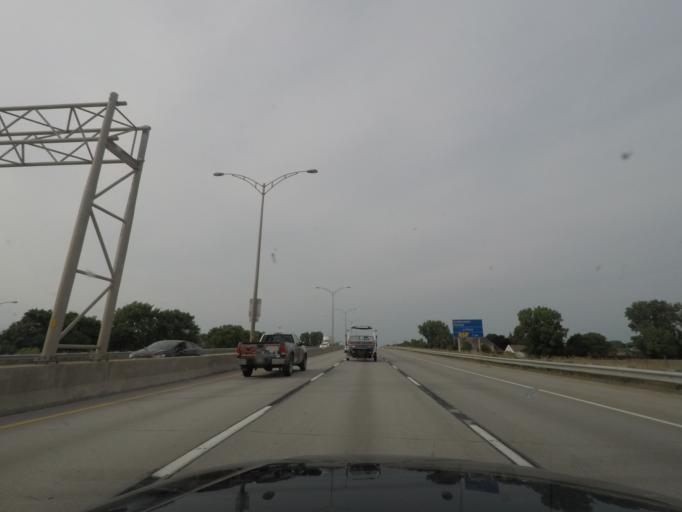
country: CA
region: Quebec
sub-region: Monteregie
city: La Prairie
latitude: 45.4065
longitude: -73.5066
